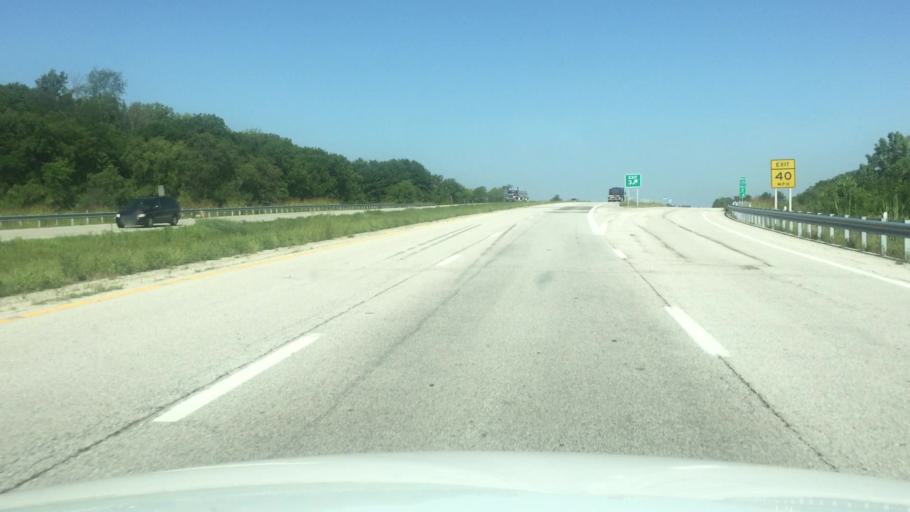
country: US
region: Missouri
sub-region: Buchanan County
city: Saint Joseph
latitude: 39.7197
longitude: -94.8298
